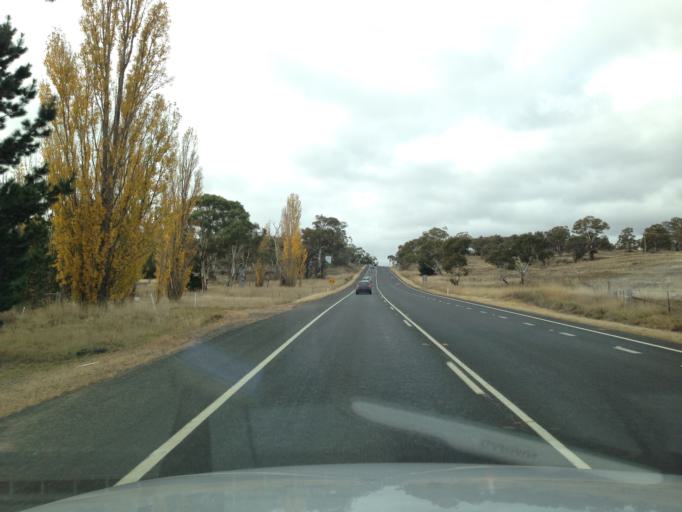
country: AU
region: New South Wales
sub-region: Cooma-Monaro
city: Cooma
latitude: -36.2408
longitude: 149.0689
